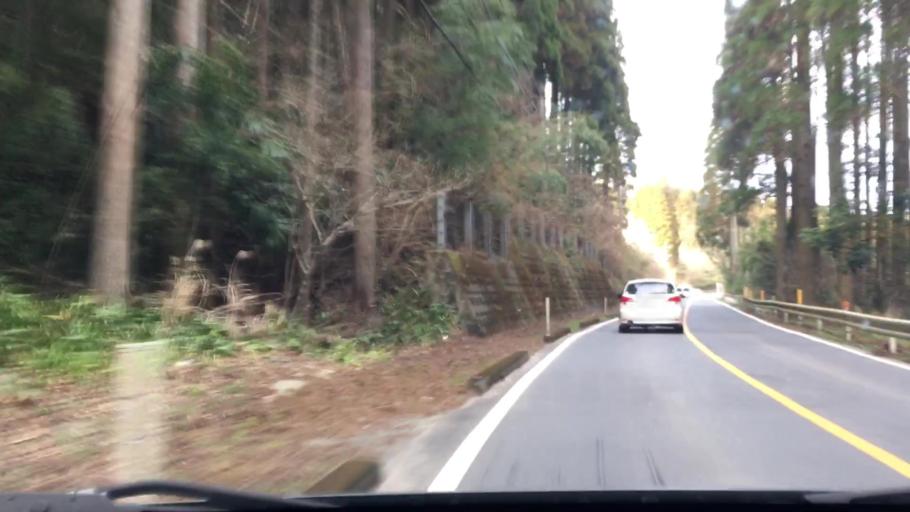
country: JP
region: Miyazaki
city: Nichinan
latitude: 31.7279
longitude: 131.3302
